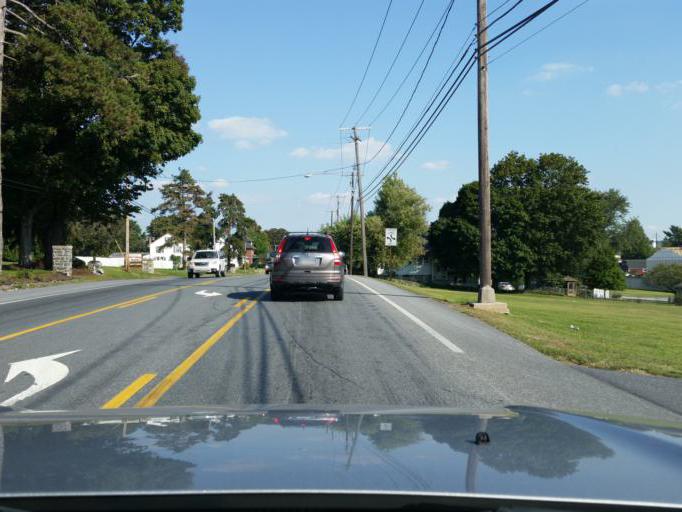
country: US
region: Pennsylvania
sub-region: Lancaster County
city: Paradise
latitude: 40.0054
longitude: -76.1080
